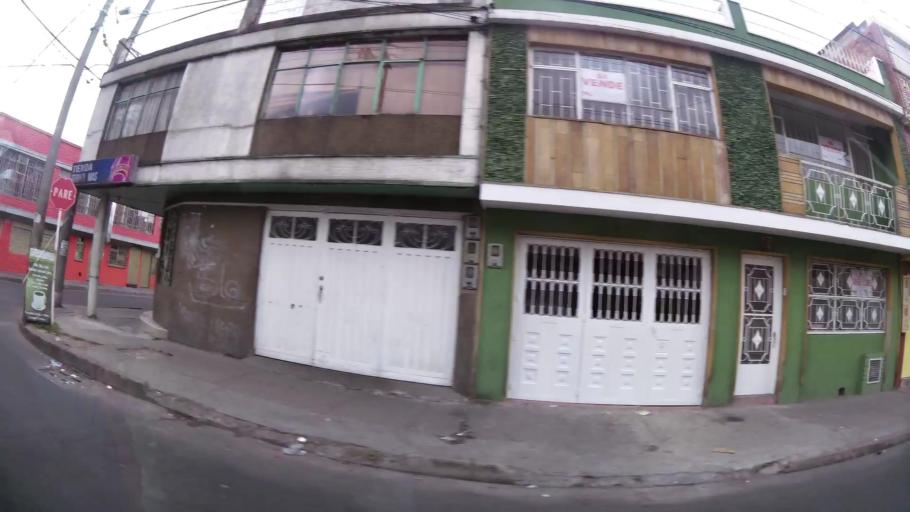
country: CO
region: Bogota D.C.
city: Bogota
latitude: 4.6250
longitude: -74.1139
